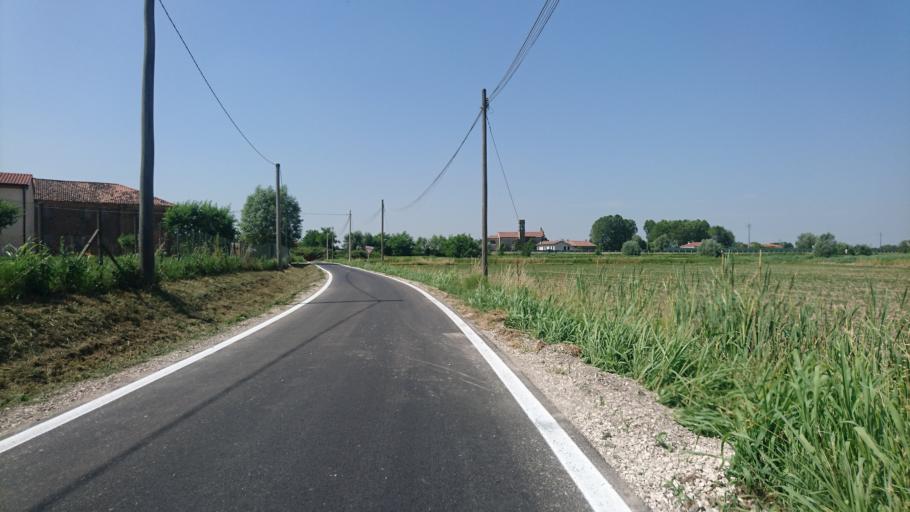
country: IT
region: Veneto
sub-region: Provincia di Padova
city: Sant'Elena
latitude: 45.2136
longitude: 11.7176
